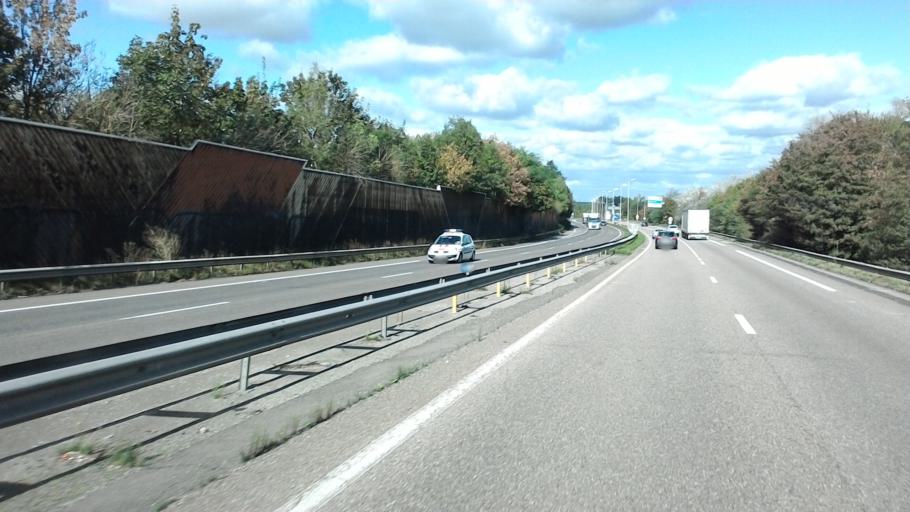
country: FR
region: Lorraine
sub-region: Departement de Meurthe-et-Moselle
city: Dommartin-les-Toul
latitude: 48.6710
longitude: 5.9185
